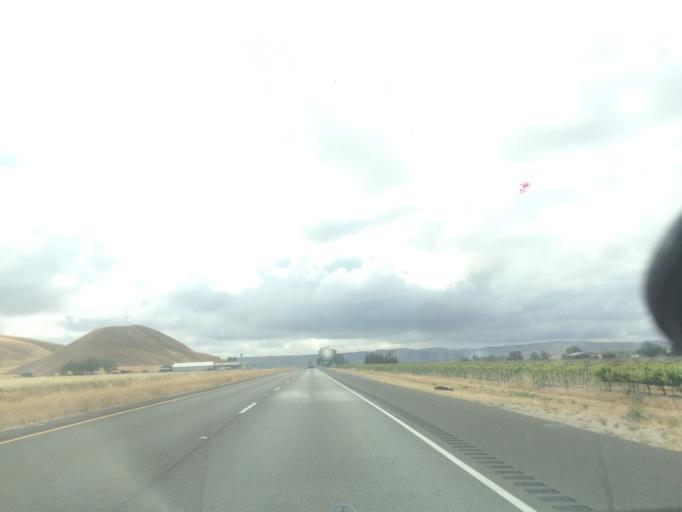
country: US
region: California
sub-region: San Luis Obispo County
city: Shandon
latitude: 35.6614
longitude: -120.4207
